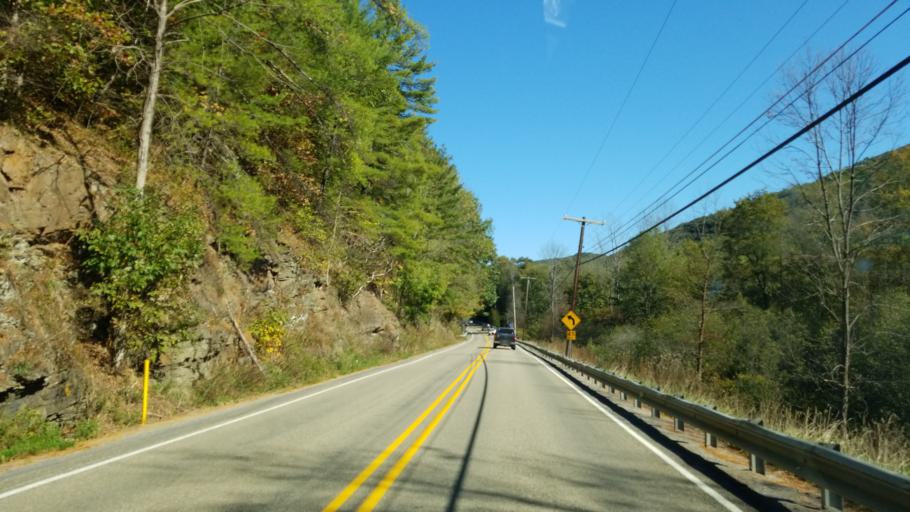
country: US
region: Pennsylvania
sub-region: Elk County
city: Saint Marys
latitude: 41.2814
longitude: -78.4485
